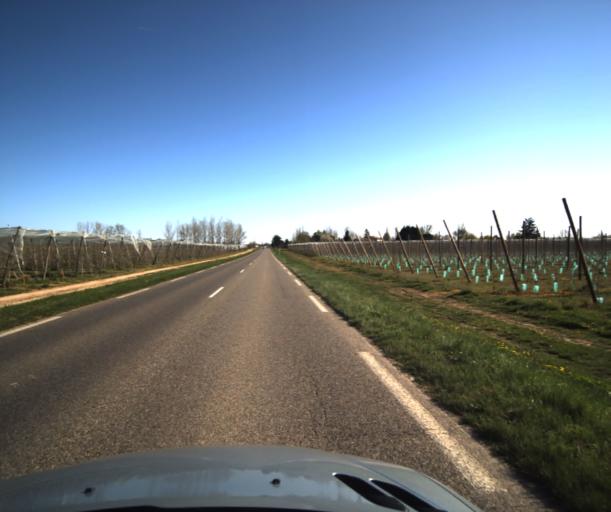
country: FR
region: Midi-Pyrenees
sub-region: Departement du Tarn-et-Garonne
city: Corbarieu
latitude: 43.9408
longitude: 1.3561
